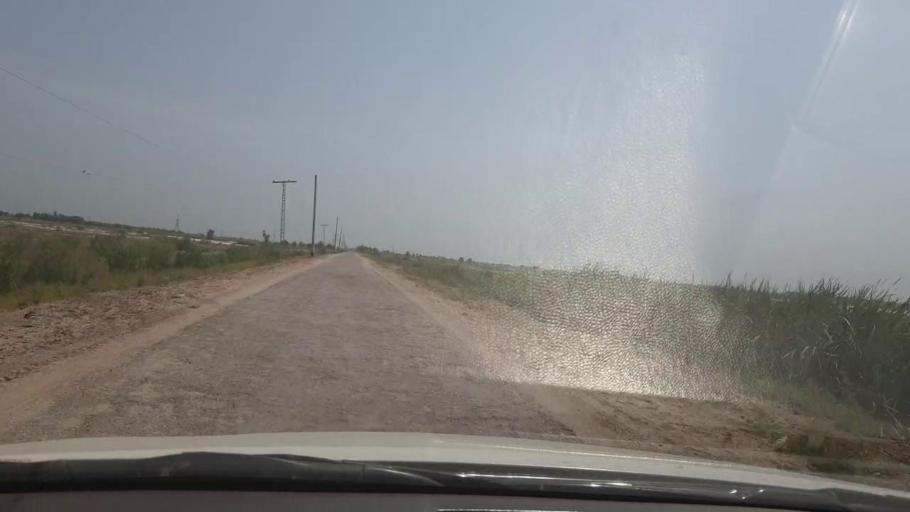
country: PK
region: Sindh
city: Garhi Yasin
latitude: 27.9529
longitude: 68.5058
